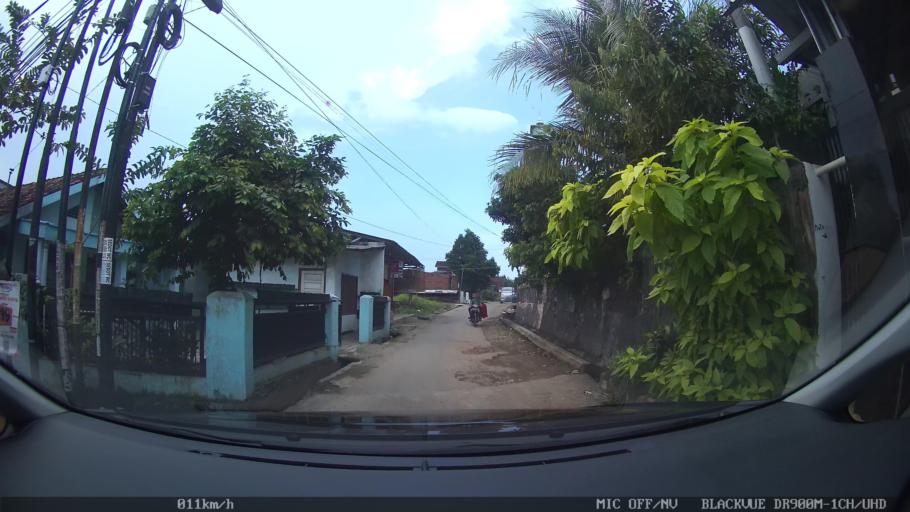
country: ID
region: Lampung
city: Kedaton
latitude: -5.3930
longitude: 105.2090
